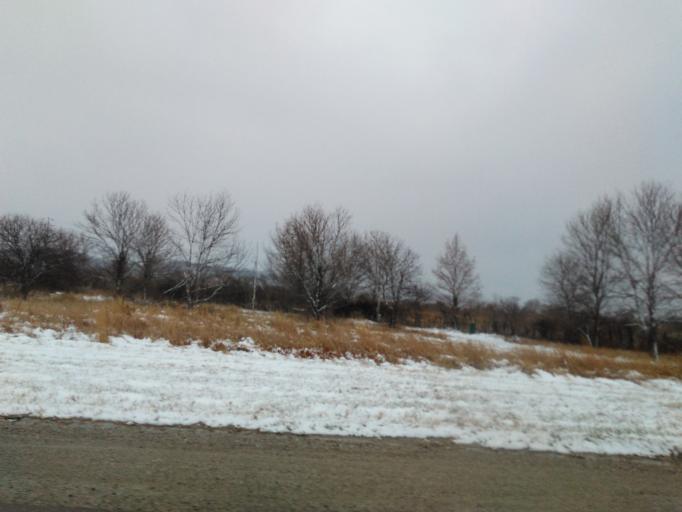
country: US
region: Illinois
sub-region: Saint Clair County
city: Caseyville
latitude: 38.6732
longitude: -90.0272
